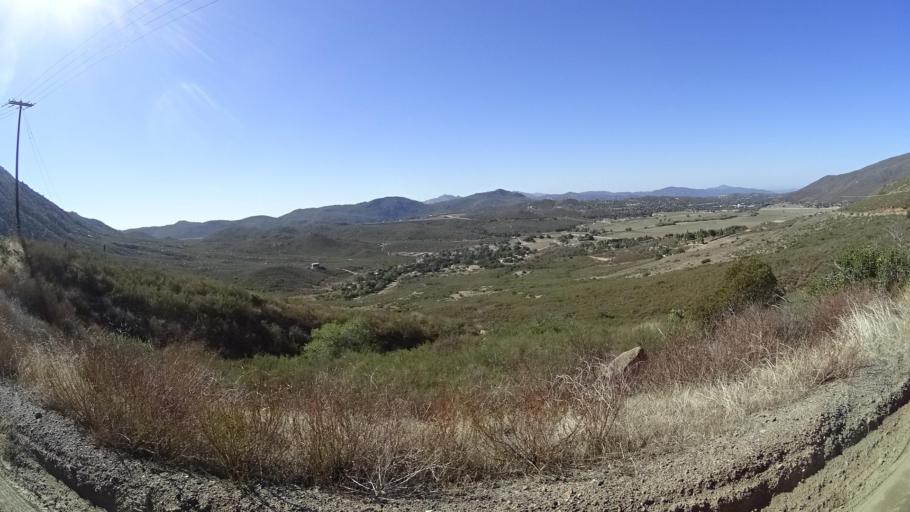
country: US
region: California
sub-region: San Diego County
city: Descanso
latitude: 32.8612
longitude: -116.6725
